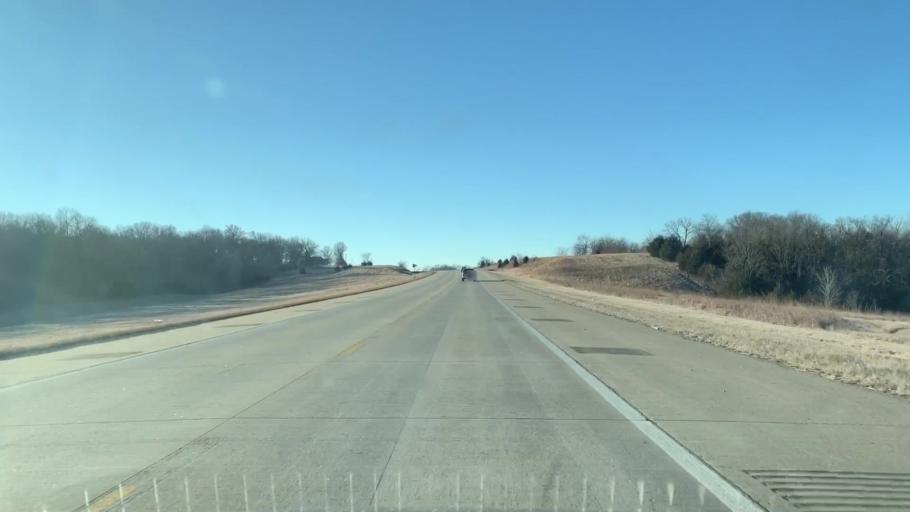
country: US
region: Kansas
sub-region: Crawford County
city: Arma
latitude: 37.5828
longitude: -94.7056
